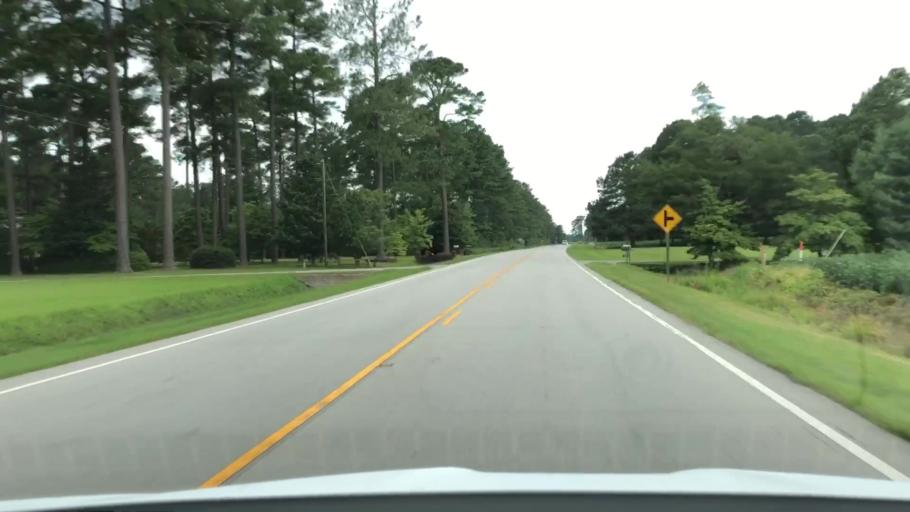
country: US
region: North Carolina
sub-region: Jones County
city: Trenton
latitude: 35.0734
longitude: -77.3835
